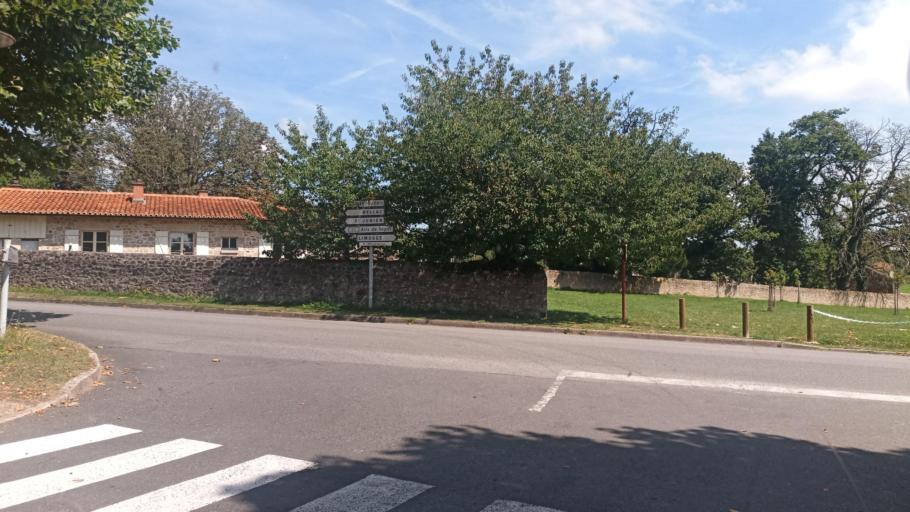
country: FR
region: Limousin
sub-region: Departement de la Haute-Vienne
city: Oradour-sur-Glane
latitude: 45.9311
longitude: 1.0346
